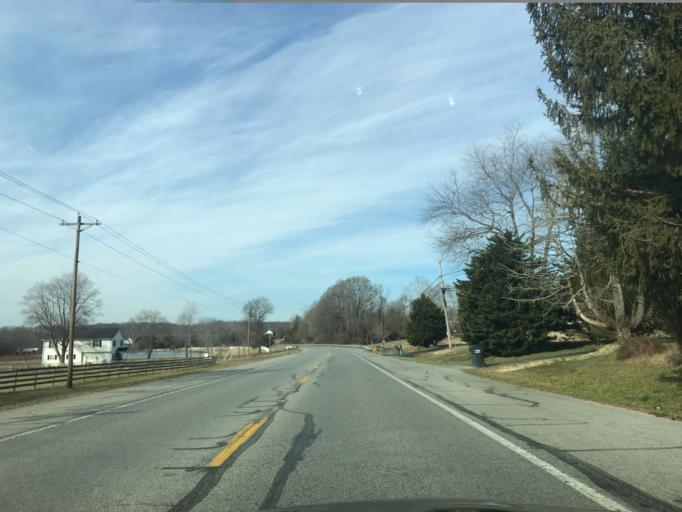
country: US
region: Maryland
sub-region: Charles County
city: La Plata
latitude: 38.5219
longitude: -77.0032
